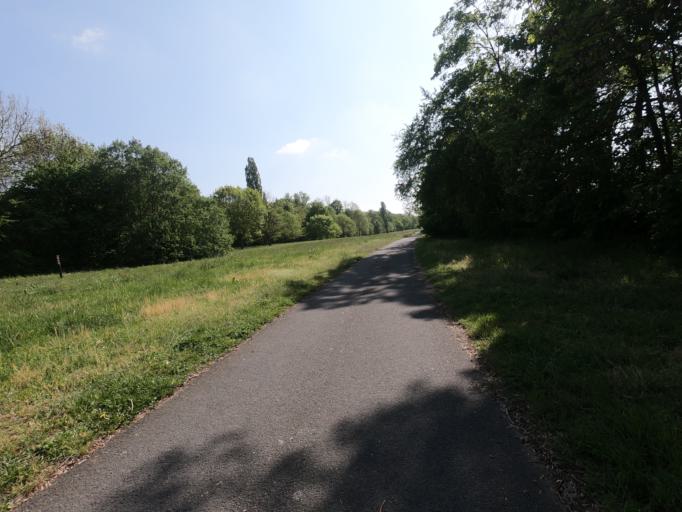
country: DE
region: Hesse
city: Kelsterbach
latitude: 50.0534
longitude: 8.5098
